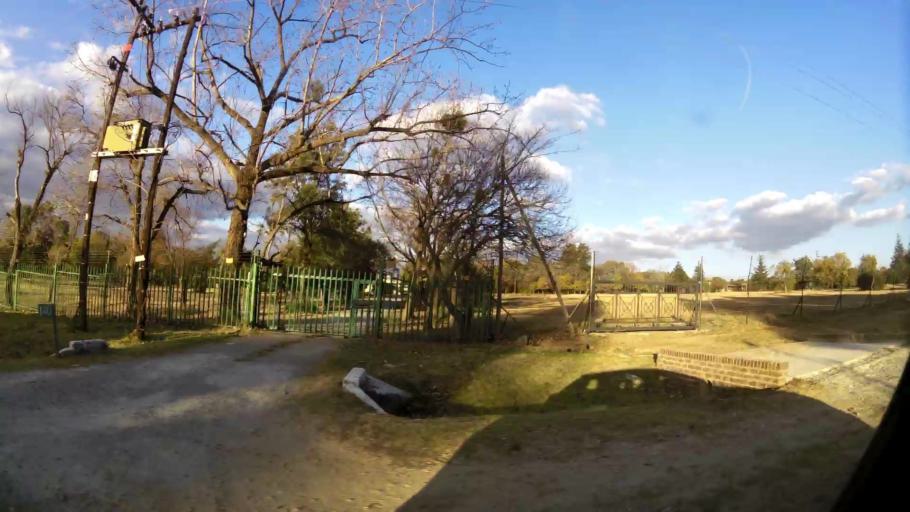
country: ZA
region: Gauteng
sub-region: City of Johannesburg Metropolitan Municipality
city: Midrand
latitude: -25.9651
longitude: 28.1537
